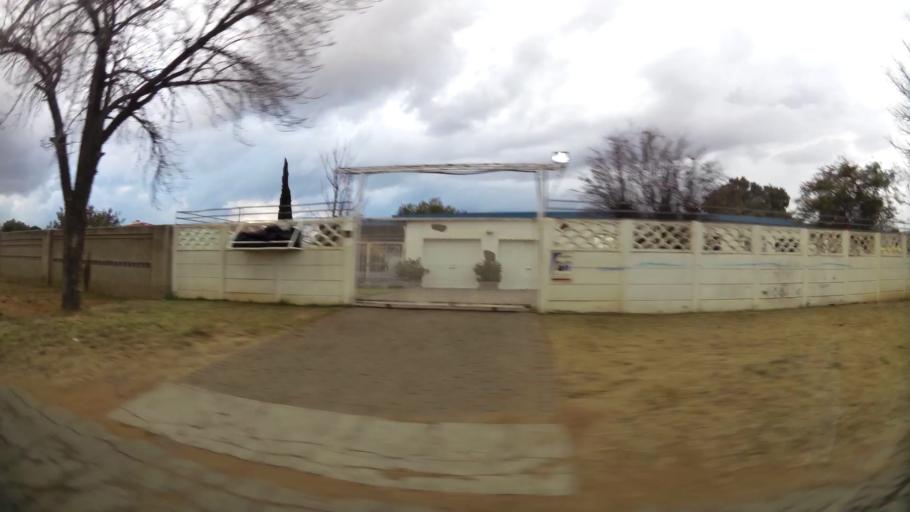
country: ZA
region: Orange Free State
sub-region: Lejweleputswa District Municipality
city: Welkom
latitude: -27.9649
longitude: 26.7232
